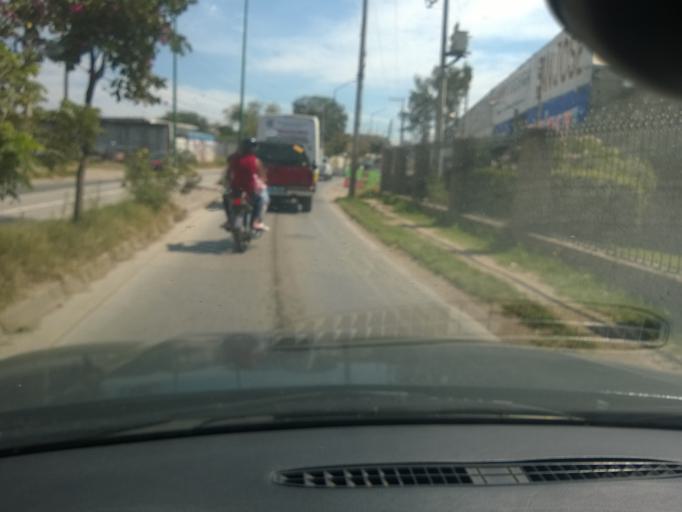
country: MX
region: Guanajuato
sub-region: Leon
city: Ejido la Joya
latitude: 21.1401
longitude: -101.7412
